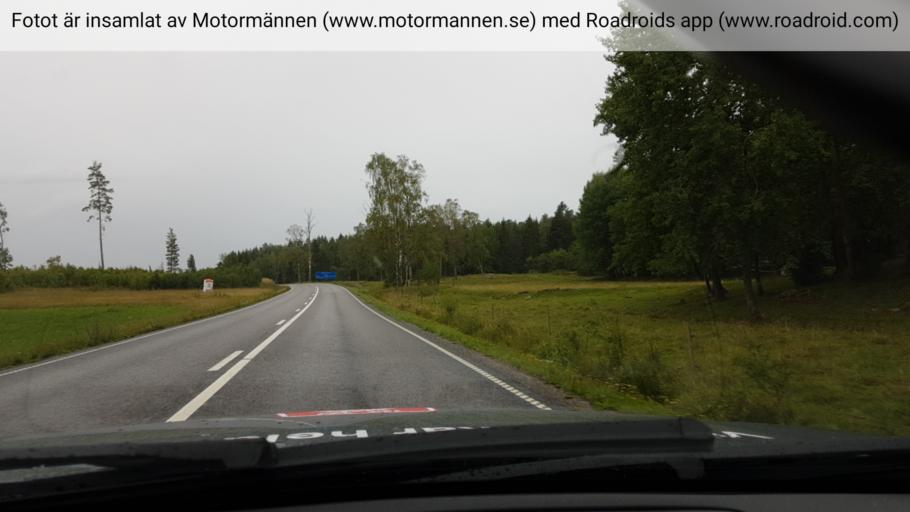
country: SE
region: Soedermanland
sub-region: Eskilstuna Kommun
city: Skogstorp
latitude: 59.3227
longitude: 16.5305
